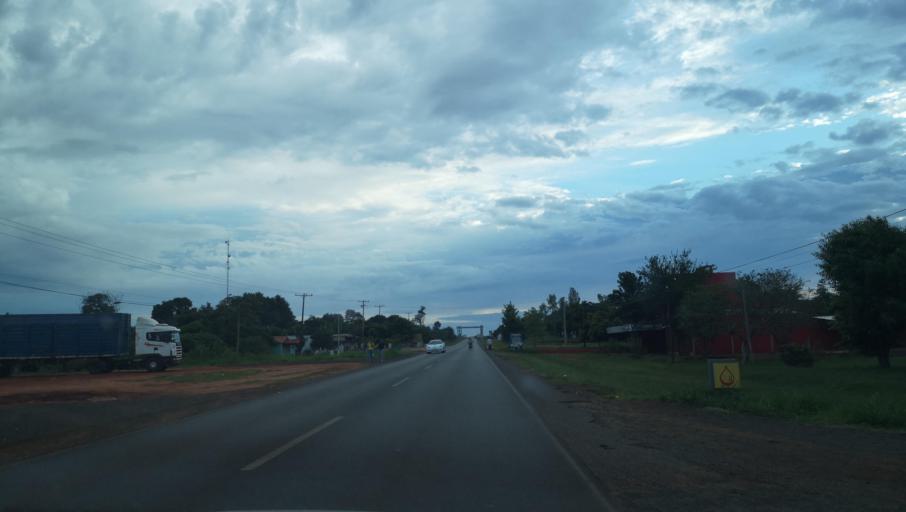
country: PY
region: San Pedro
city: Capiibary
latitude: -24.7156
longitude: -56.0131
